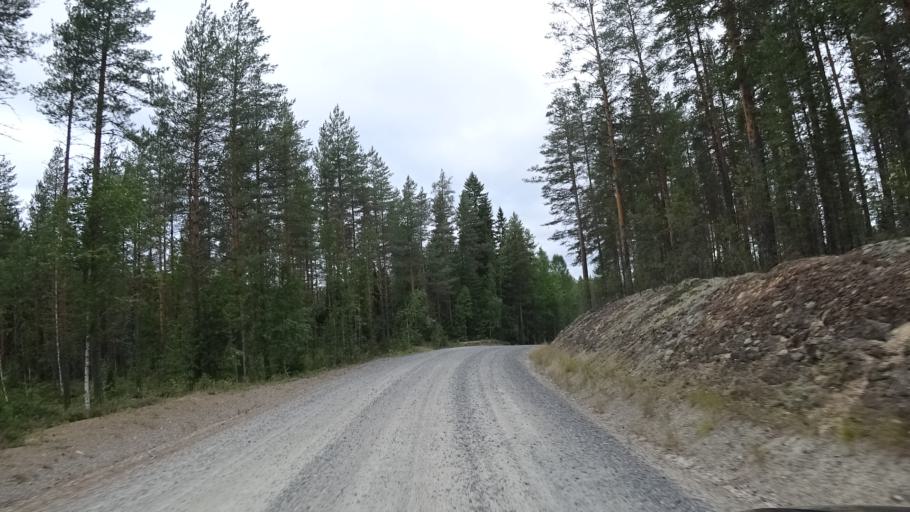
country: FI
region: North Karelia
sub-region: Pielisen Karjala
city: Lieksa
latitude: 63.2391
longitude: 30.3519
